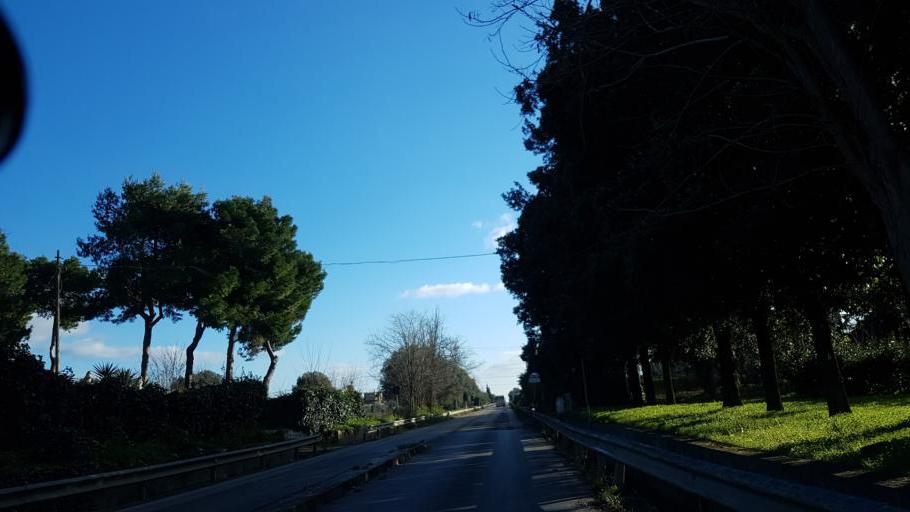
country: IT
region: Apulia
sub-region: Provincia di Brindisi
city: La Rosa
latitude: 40.6093
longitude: 17.9538
